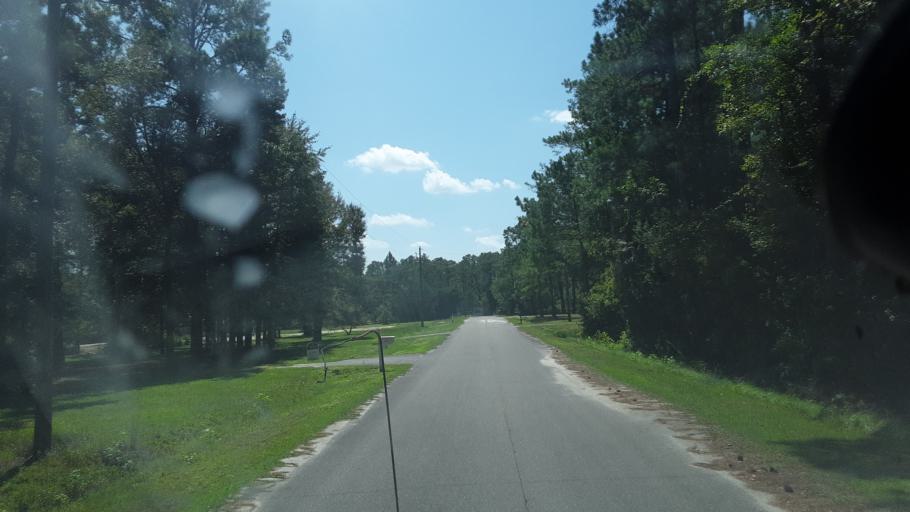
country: US
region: South Carolina
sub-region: Horry County
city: Forestbrook
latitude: 33.8383
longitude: -78.8622
